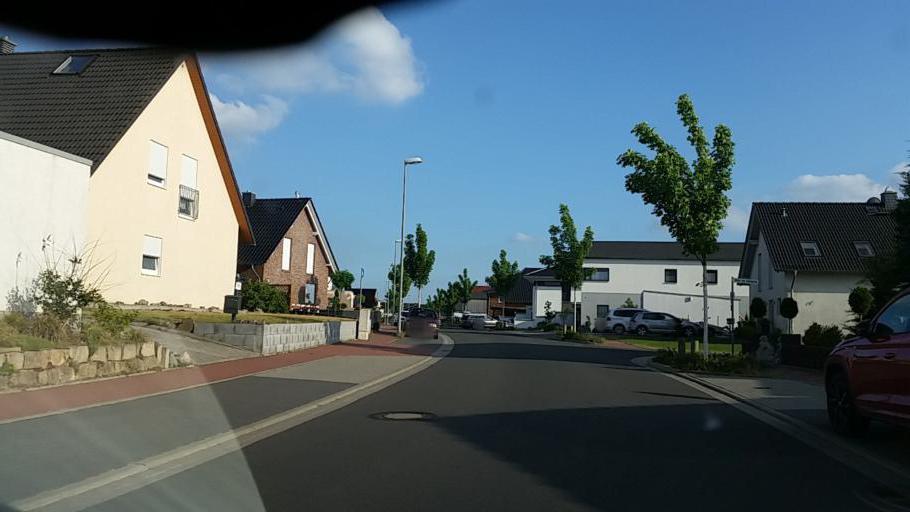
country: DE
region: Lower Saxony
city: Weyhausen
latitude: 52.4023
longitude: 10.7025
